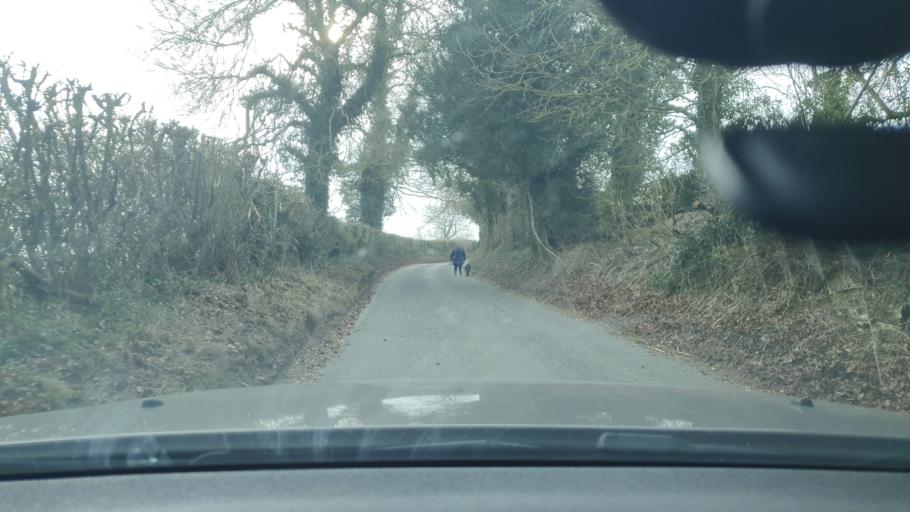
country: GB
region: England
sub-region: Wiltshire
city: Ramsbury
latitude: 51.4529
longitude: -1.5940
